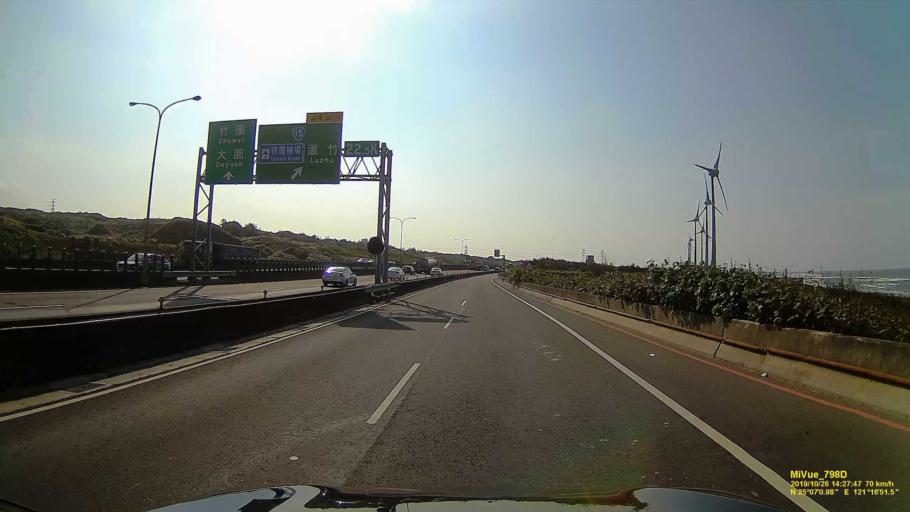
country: TW
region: Taiwan
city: Taoyuan City
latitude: 25.1170
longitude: 121.2808
